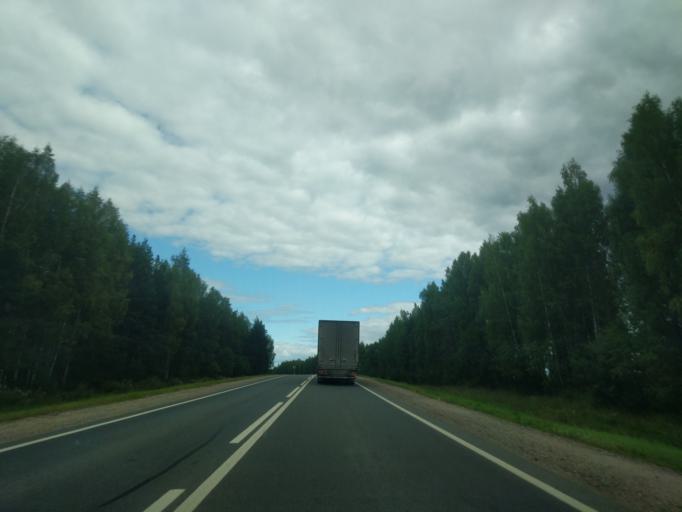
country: RU
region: Kostroma
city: Ostrovskoye
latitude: 57.8171
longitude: 42.2089
